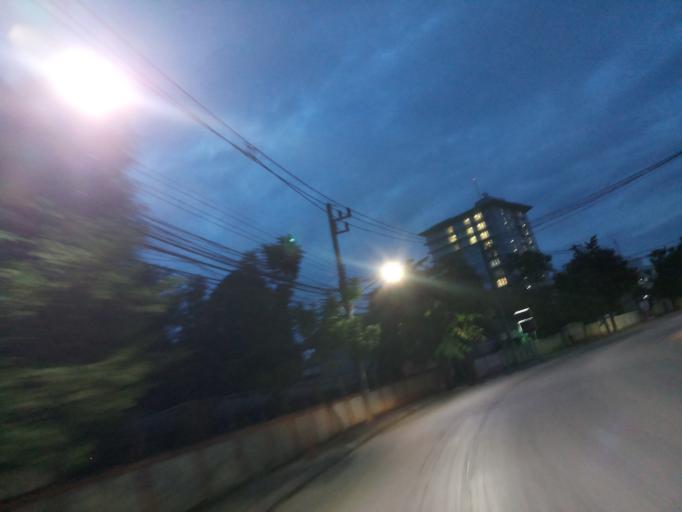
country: TH
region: Chiang Rai
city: Chiang Rai
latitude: 19.8999
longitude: 99.8261
